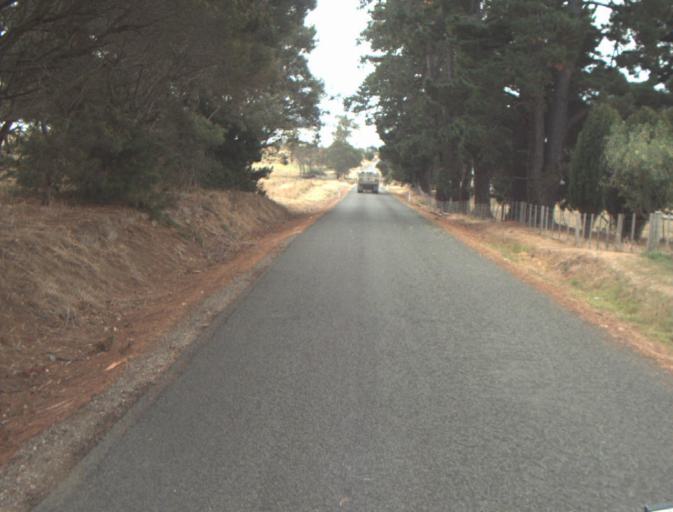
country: AU
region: Tasmania
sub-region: Launceston
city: Mayfield
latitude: -41.2929
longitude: 147.0066
